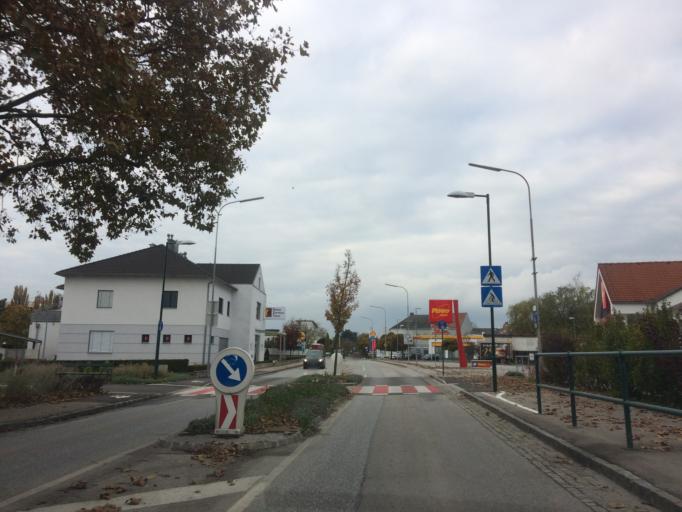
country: AT
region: Lower Austria
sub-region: Politischer Bezirk Tulln
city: Tulln
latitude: 48.3253
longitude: 16.0591
